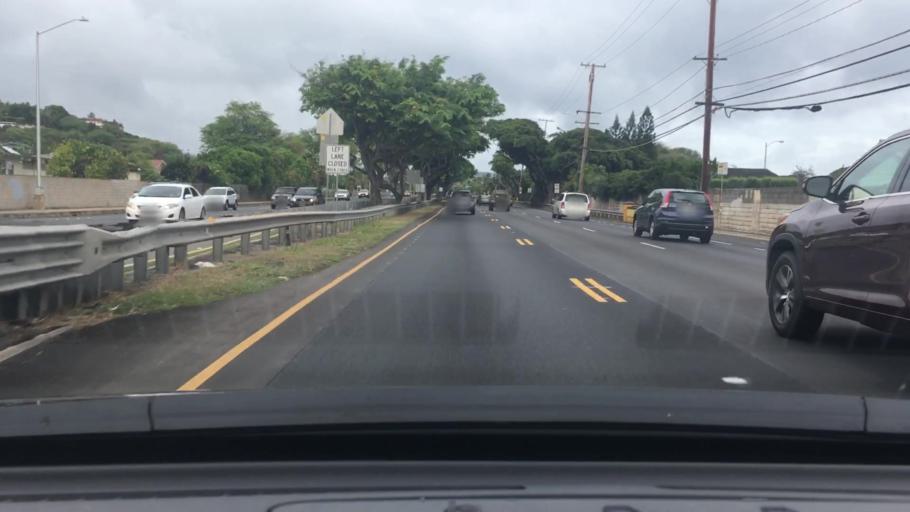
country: US
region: Hawaii
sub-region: Honolulu County
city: Waimanalo
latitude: 21.2769
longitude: -157.7720
